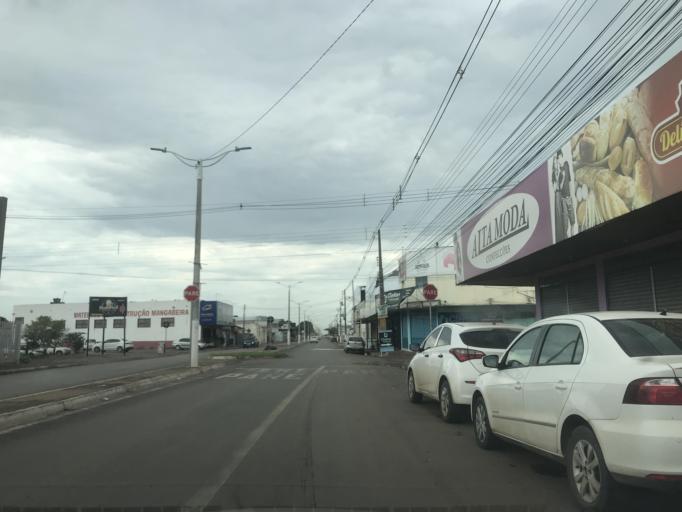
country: BR
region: Goias
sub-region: Luziania
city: Luziania
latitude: -16.2044
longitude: -47.9246
